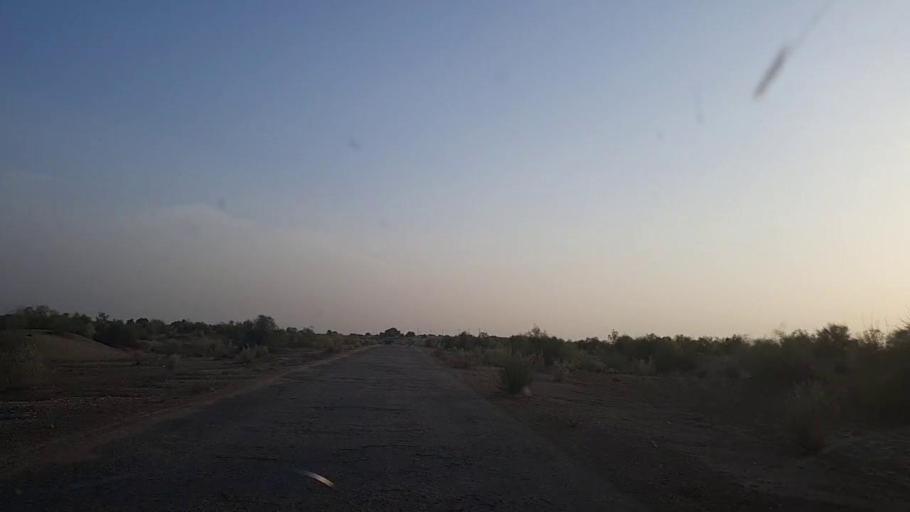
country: PK
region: Sindh
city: Khanpur
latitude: 27.6013
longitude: 69.4307
